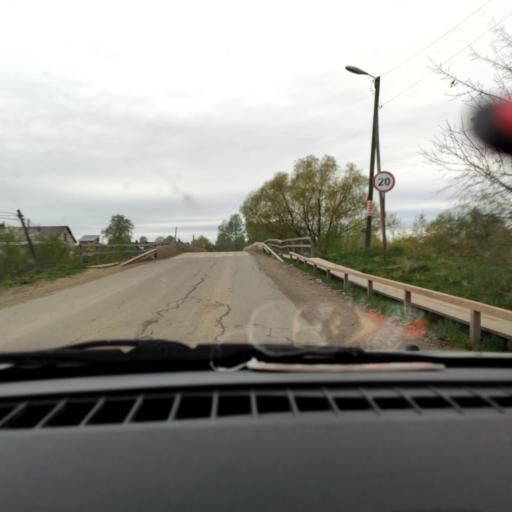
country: RU
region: Perm
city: Kudymkar
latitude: 59.0077
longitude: 54.6488
